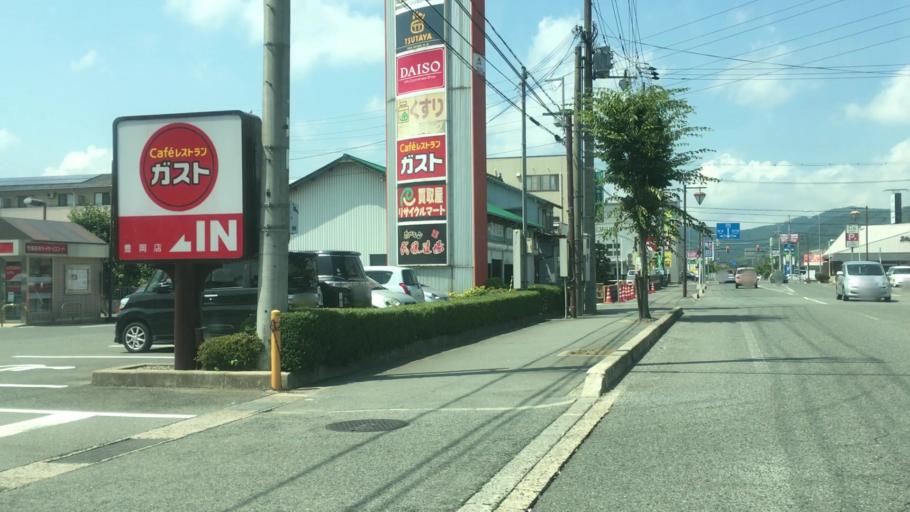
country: JP
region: Hyogo
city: Toyooka
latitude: 35.5529
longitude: 134.8155
